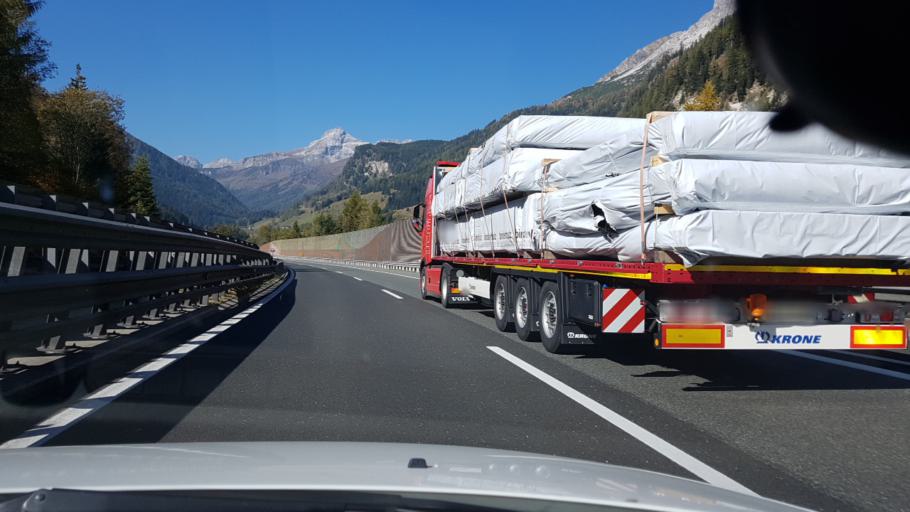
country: AT
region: Salzburg
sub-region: Politischer Bezirk Tamsweg
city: Zederhaus
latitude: 47.1620
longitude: 13.4807
